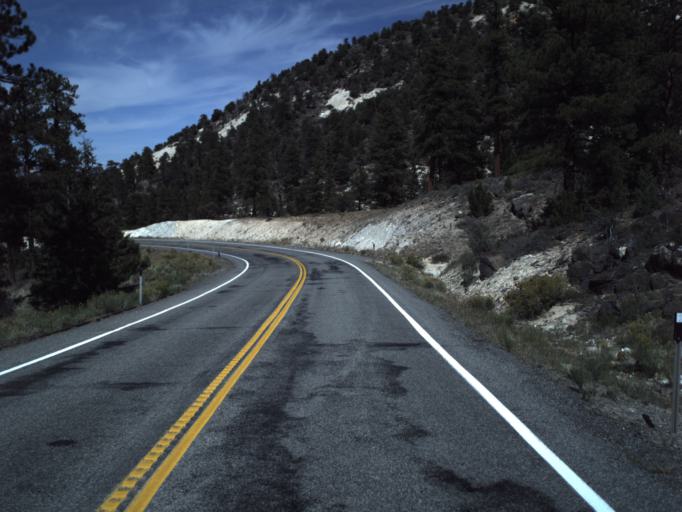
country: US
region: Utah
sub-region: Wayne County
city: Loa
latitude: 38.1826
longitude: -111.3495
